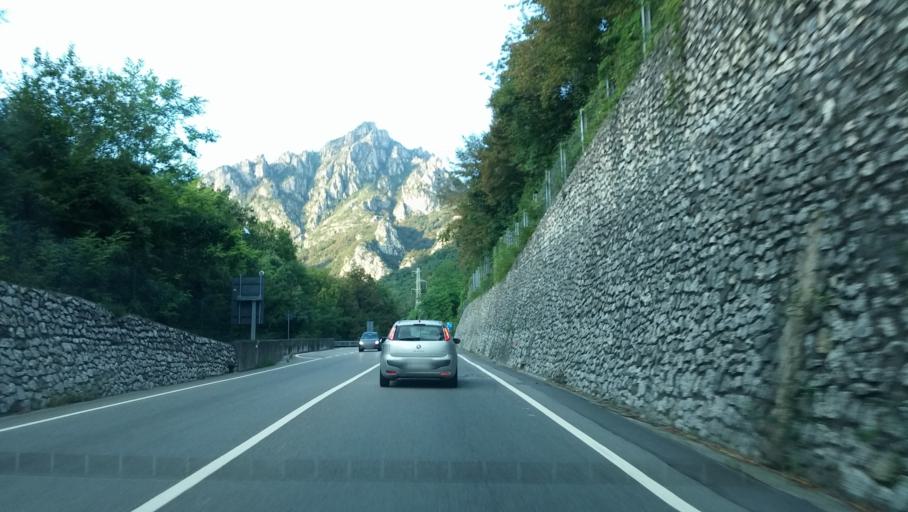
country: IT
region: Lombardy
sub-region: Provincia di Lecco
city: Ballabio
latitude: 45.8673
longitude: 9.4254
